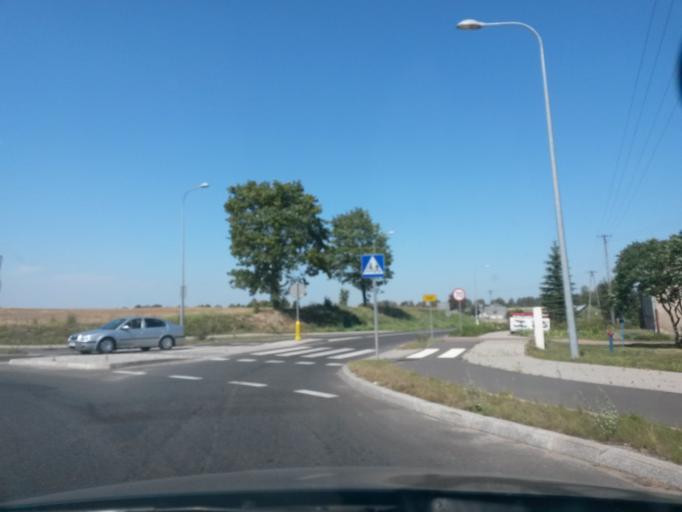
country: PL
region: Warmian-Masurian Voivodeship
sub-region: Powiat ilawski
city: Lubawa
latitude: 53.4079
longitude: 19.7965
